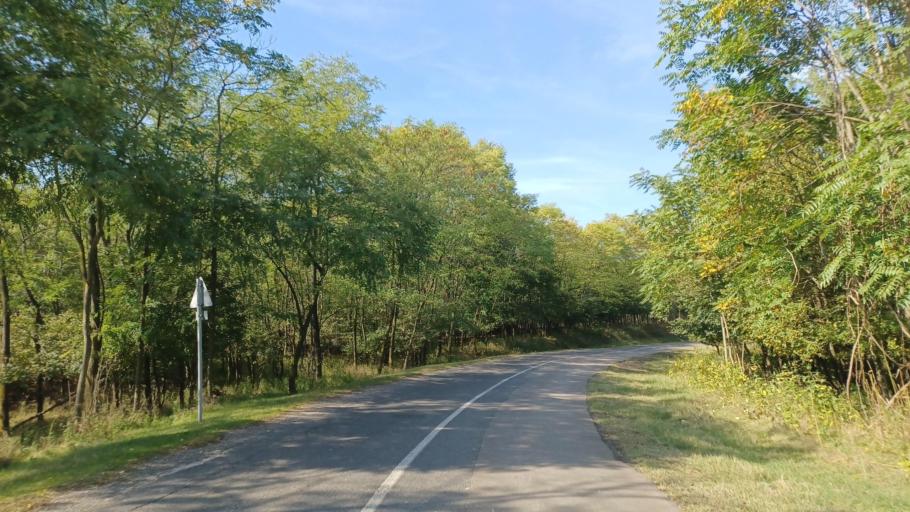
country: HU
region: Tolna
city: Pincehely
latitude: 46.6656
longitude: 18.4812
